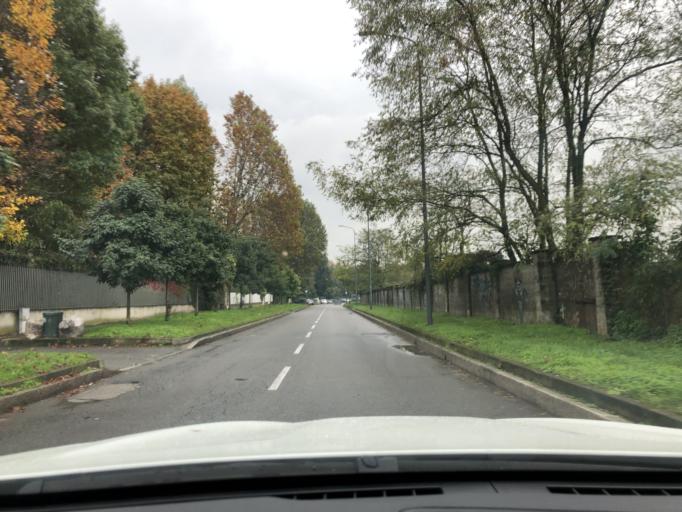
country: IT
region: Lombardy
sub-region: Citta metropolitana di Milano
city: Figino
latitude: 45.4795
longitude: 9.1151
